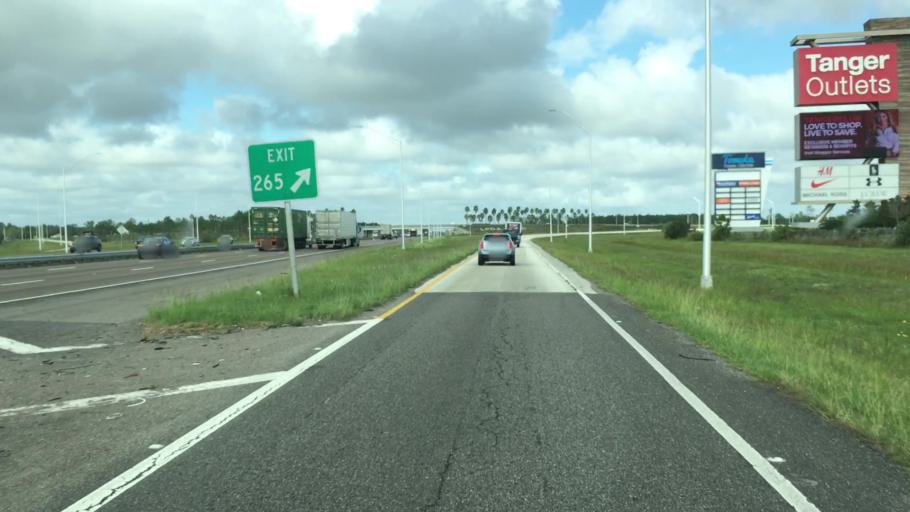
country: US
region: Florida
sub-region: Volusia County
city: Holly Hill
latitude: 29.2144
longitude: -81.1009
